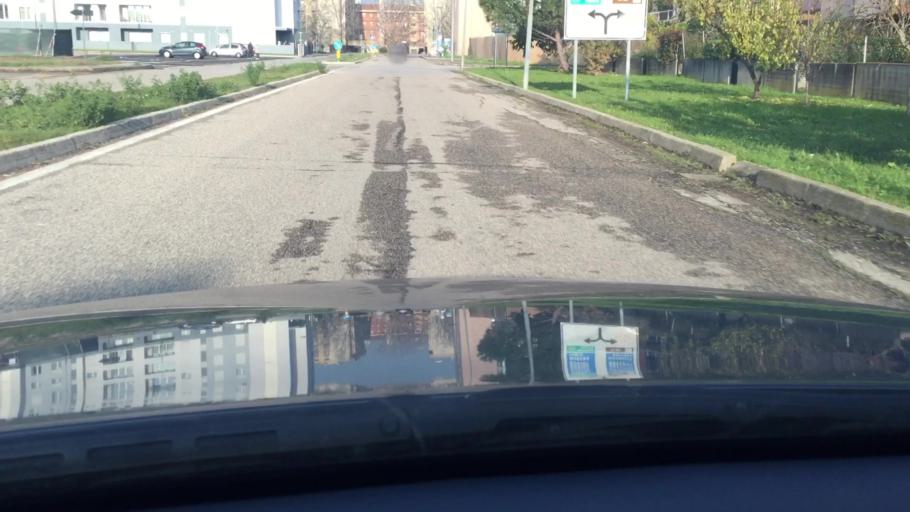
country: IT
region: Emilia-Romagna
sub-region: Provincia di Ferrara
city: Ferrara
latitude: 44.8193
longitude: 11.5967
